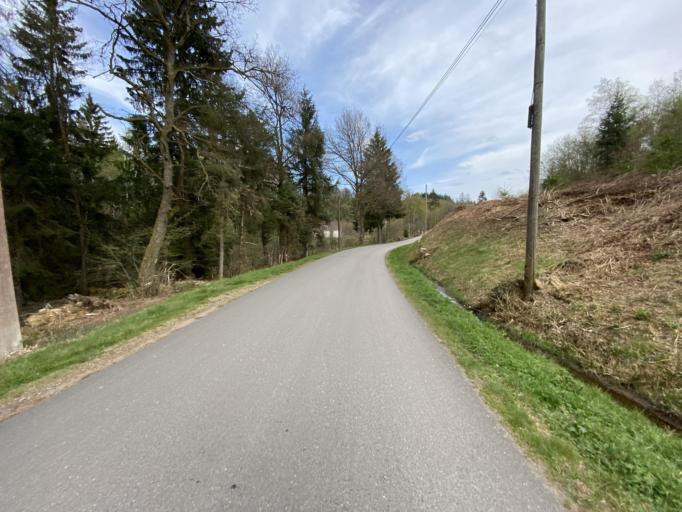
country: FR
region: Bourgogne
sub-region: Departement de la Cote-d'Or
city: Saulieu
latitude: 47.3201
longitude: 4.0584
